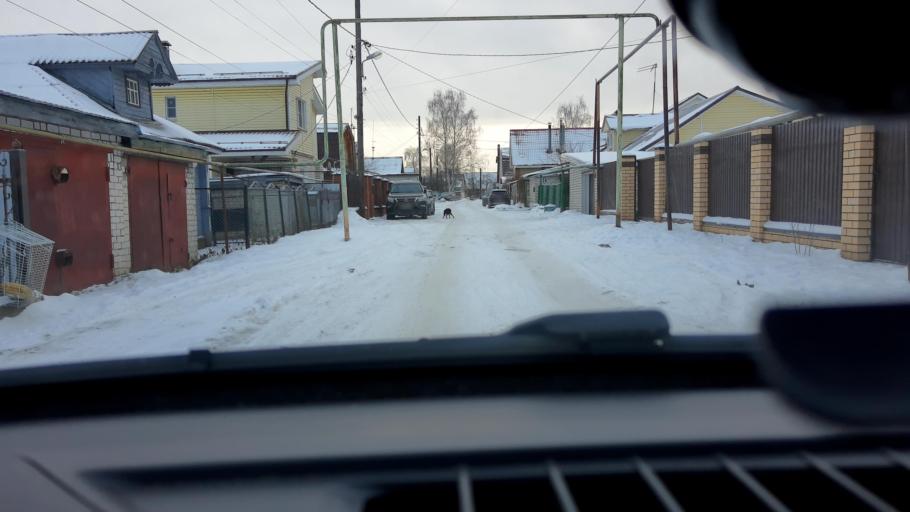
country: RU
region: Nizjnij Novgorod
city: Gorbatovka
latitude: 56.3735
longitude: 43.8262
